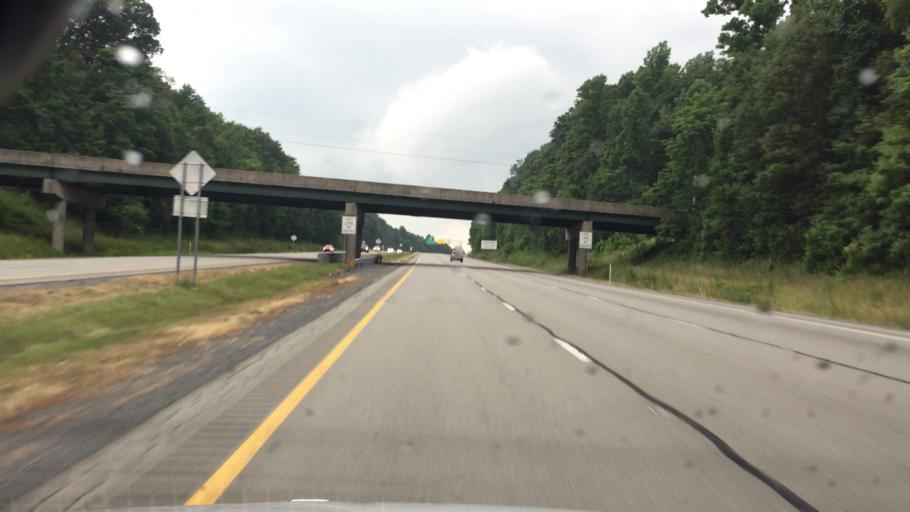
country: US
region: West Virginia
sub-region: Monongalia County
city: Cheat Lake
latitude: 39.6558
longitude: -79.7620
